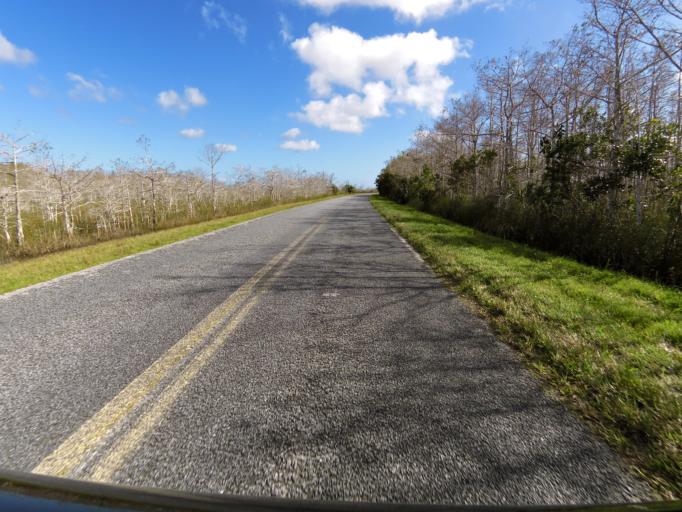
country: US
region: Florida
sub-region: Miami-Dade County
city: Florida City
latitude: 25.4315
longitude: -80.7756
